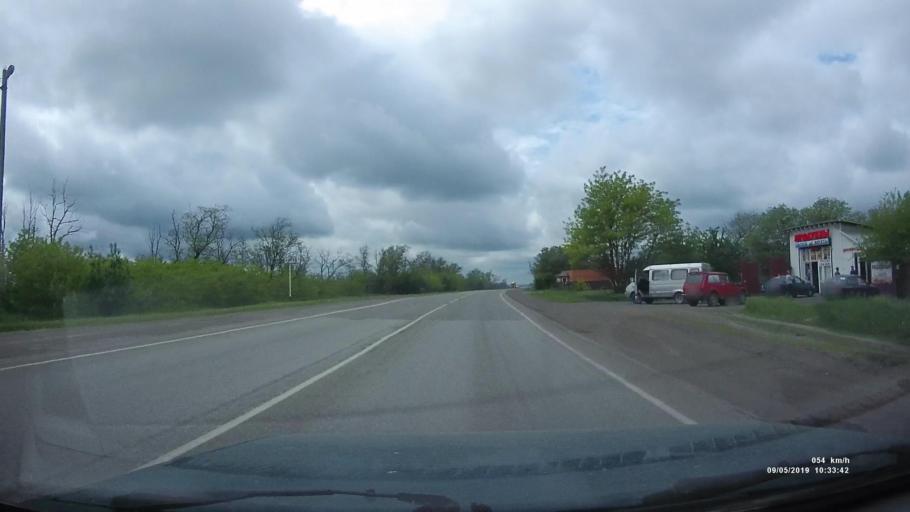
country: RU
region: Rostov
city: Azov
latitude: 47.0616
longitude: 39.4243
